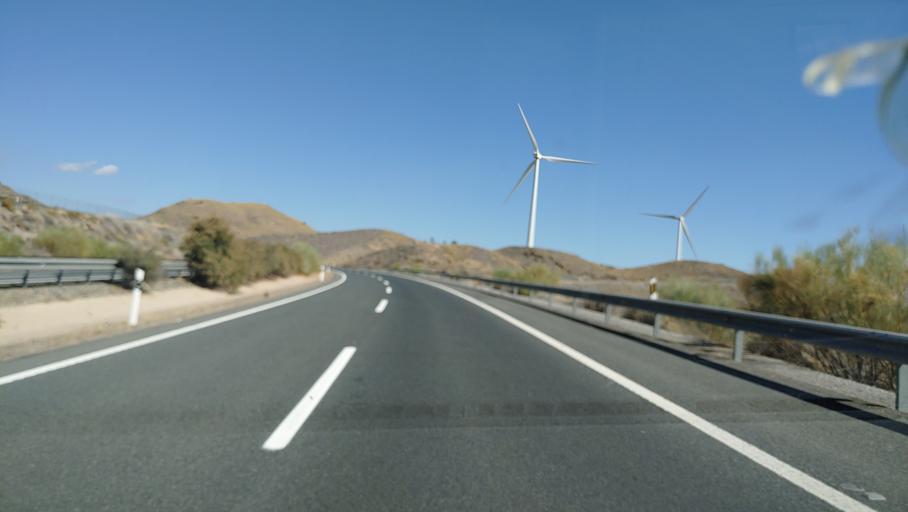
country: ES
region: Andalusia
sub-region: Provincia de Almeria
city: Abla
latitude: 37.1357
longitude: -2.6595
